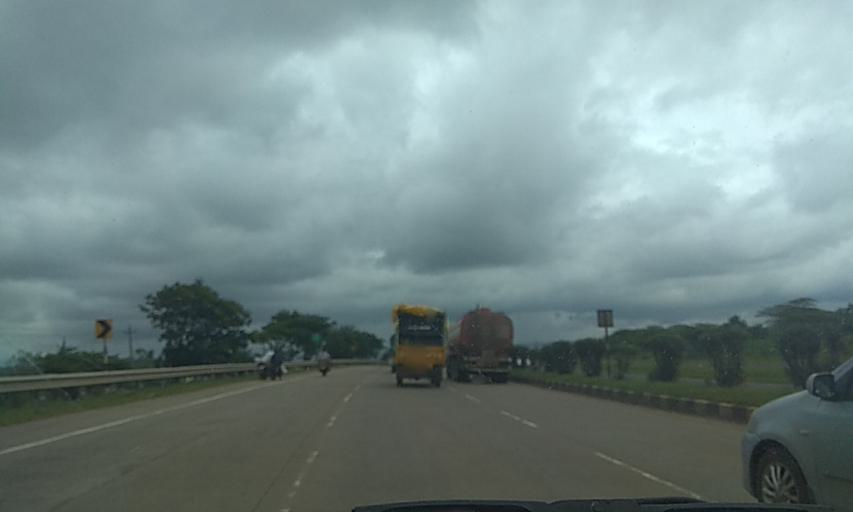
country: IN
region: Karnataka
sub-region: Belgaum
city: Belgaum
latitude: 15.8133
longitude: 74.5673
